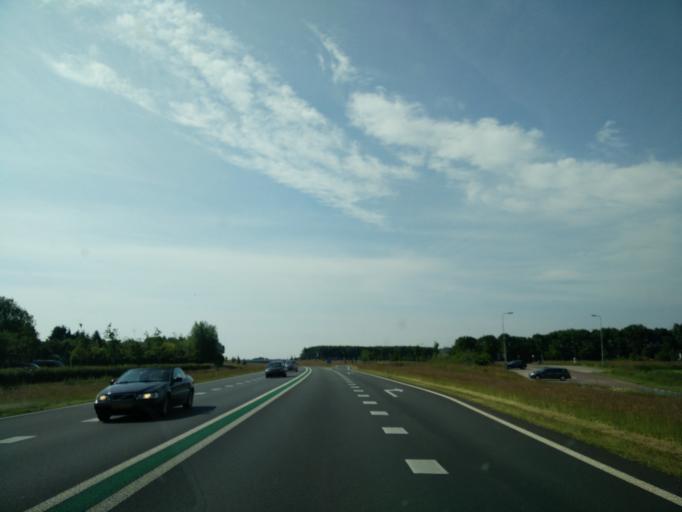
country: NL
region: Drenthe
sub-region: Gemeente Aa en Hunze
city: Anloo
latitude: 53.0030
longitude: 6.7511
